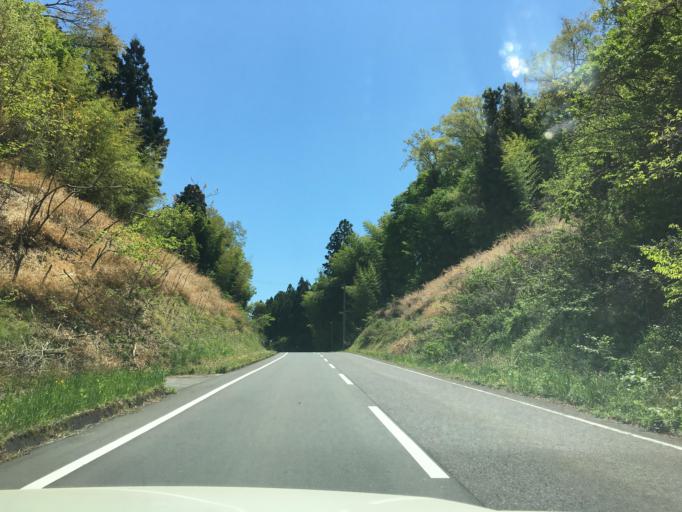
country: JP
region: Fukushima
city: Funehikimachi-funehiki
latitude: 37.3727
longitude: 140.6278
